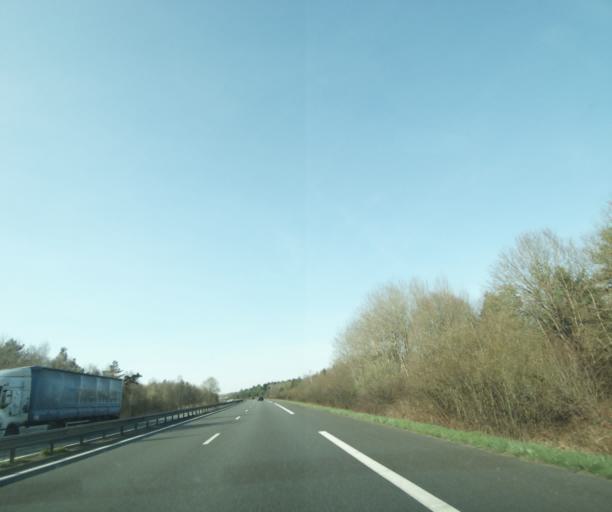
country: FR
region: Centre
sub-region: Departement du Loiret
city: La Ferte-Saint-Aubin
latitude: 47.7138
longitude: 1.8980
